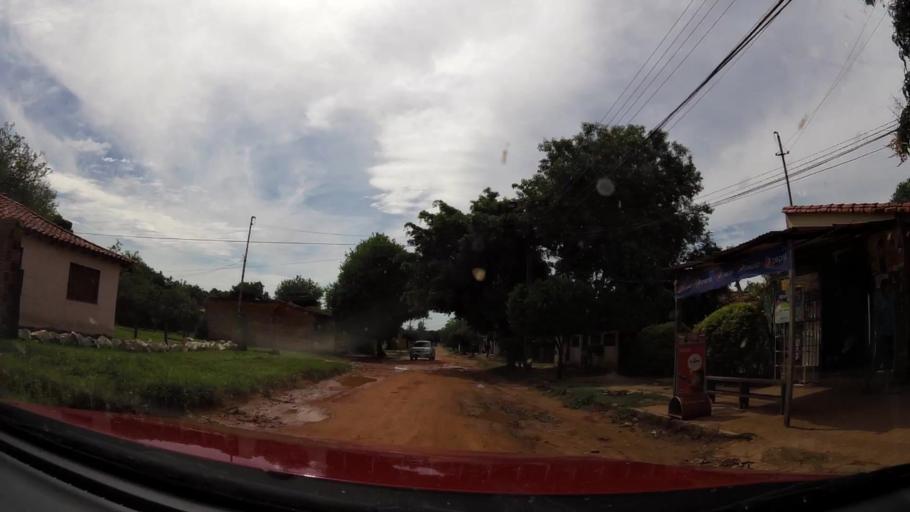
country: PY
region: Central
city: Limpio
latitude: -25.1888
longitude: -57.4755
